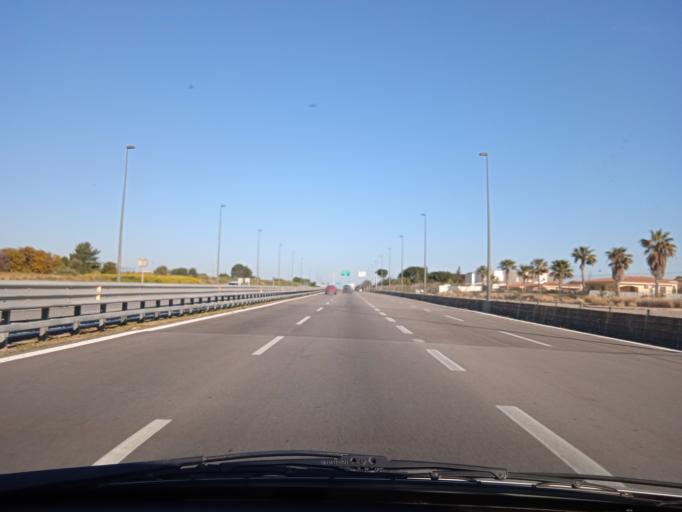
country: IT
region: Sicily
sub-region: Palermo
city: Carini
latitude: 38.1753
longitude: 13.1565
